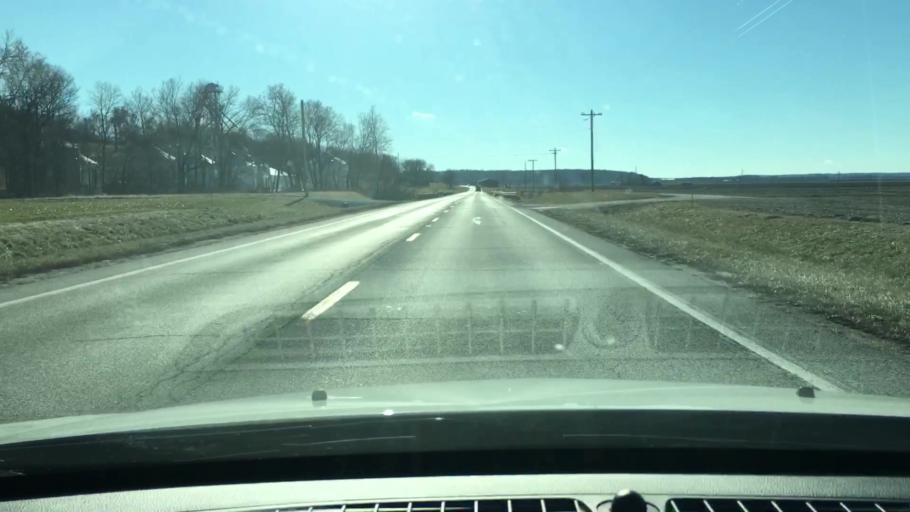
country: US
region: Illinois
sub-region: Morgan County
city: Meredosia
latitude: 39.7733
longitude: -90.5303
